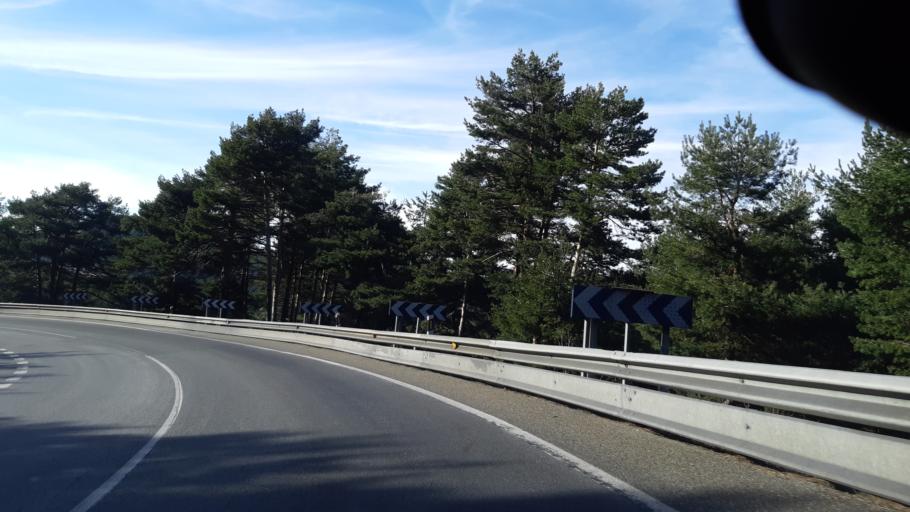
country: ES
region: Madrid
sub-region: Provincia de Madrid
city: Guadarrama
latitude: 40.7104
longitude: -4.1572
